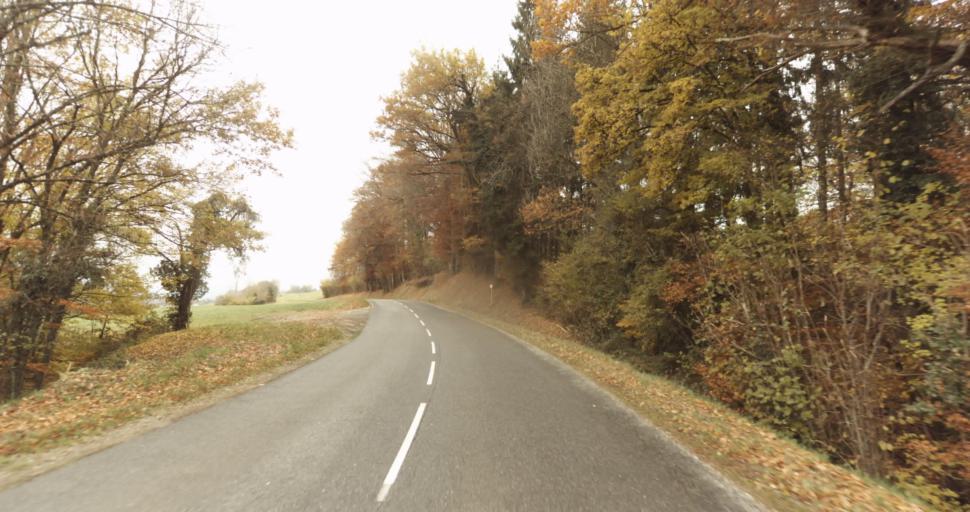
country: FR
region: Rhone-Alpes
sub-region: Departement de la Haute-Savoie
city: Evires
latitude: 46.0278
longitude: 6.2049
